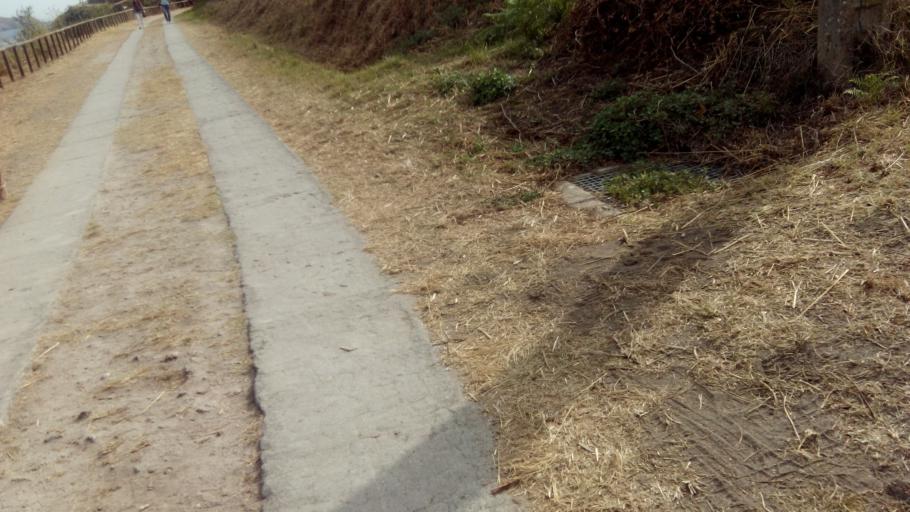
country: ES
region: Galicia
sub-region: Provincia de Pontevedra
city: Sanxenxo
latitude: 42.3703
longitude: -8.9341
